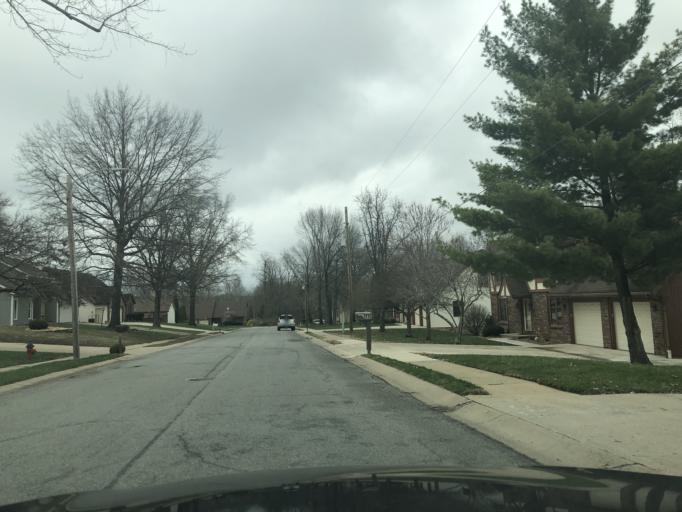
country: US
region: Kansas
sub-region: Leavenworth County
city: Leavenworth
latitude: 39.2844
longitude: -94.9137
